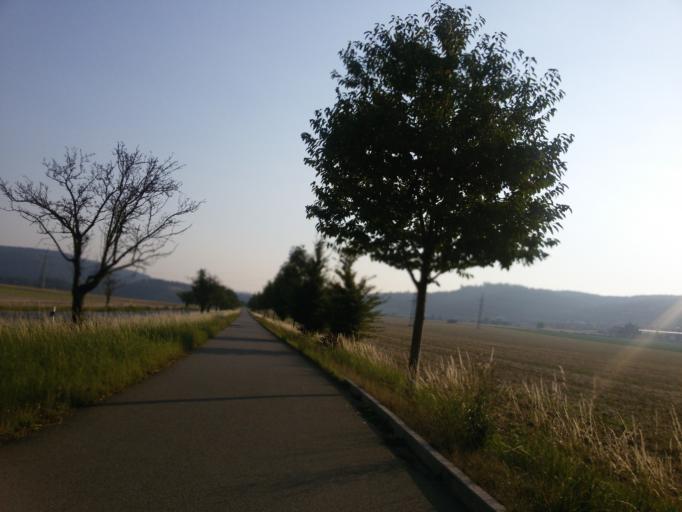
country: CZ
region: South Moravian
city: Tisnov
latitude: 49.3524
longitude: 16.4392
